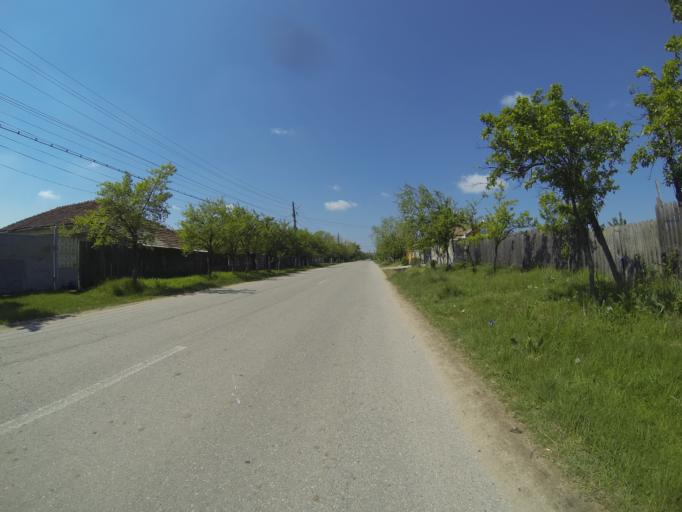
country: RO
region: Dolj
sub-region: Comuna Breasta
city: Breasta
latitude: 44.2989
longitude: 23.6514
